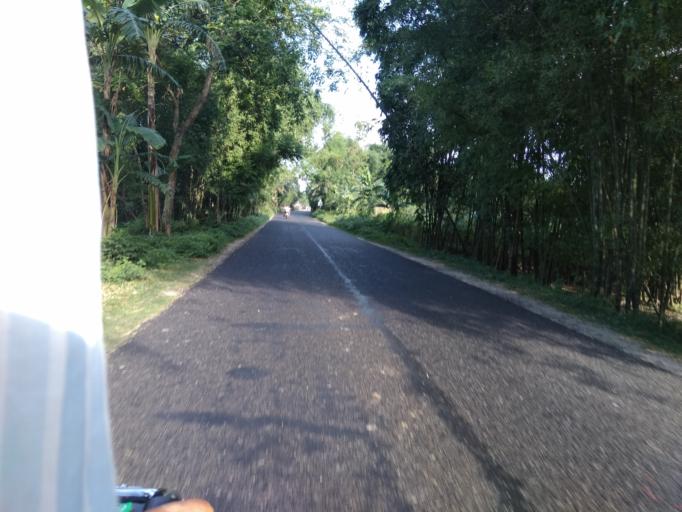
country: BD
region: Rangpur Division
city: Rangpur
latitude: 25.8314
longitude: 89.1185
